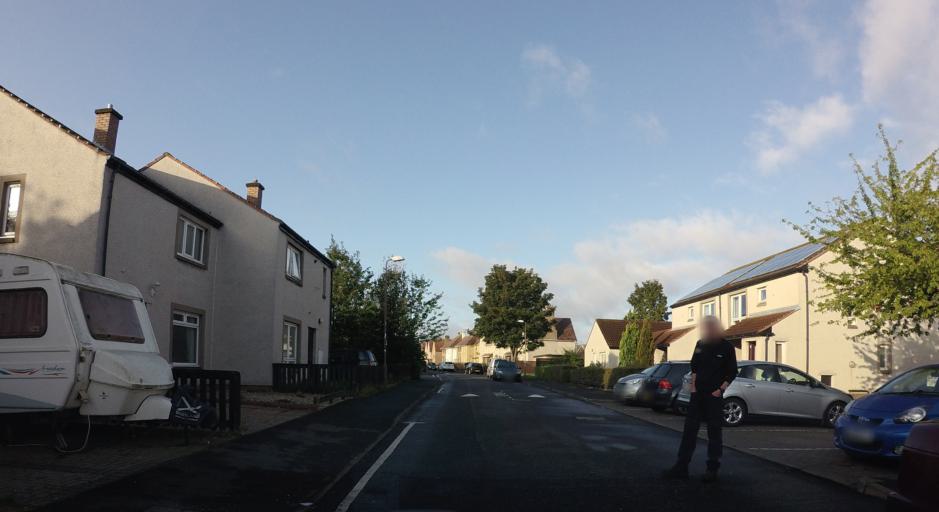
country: GB
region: Scotland
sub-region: East Lothian
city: Musselburgh
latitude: 55.9205
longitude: -3.0352
